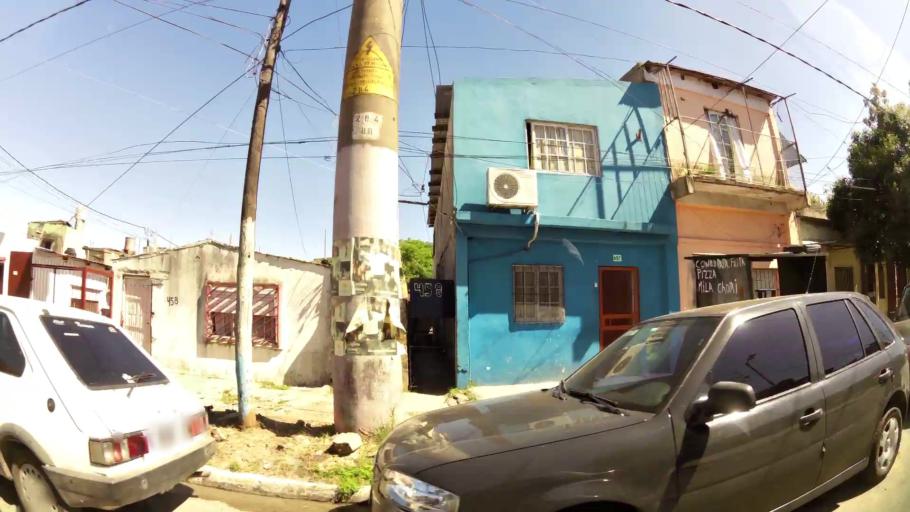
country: AR
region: Buenos Aires
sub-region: Partido de Quilmes
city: Quilmes
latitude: -34.7101
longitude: -58.2976
